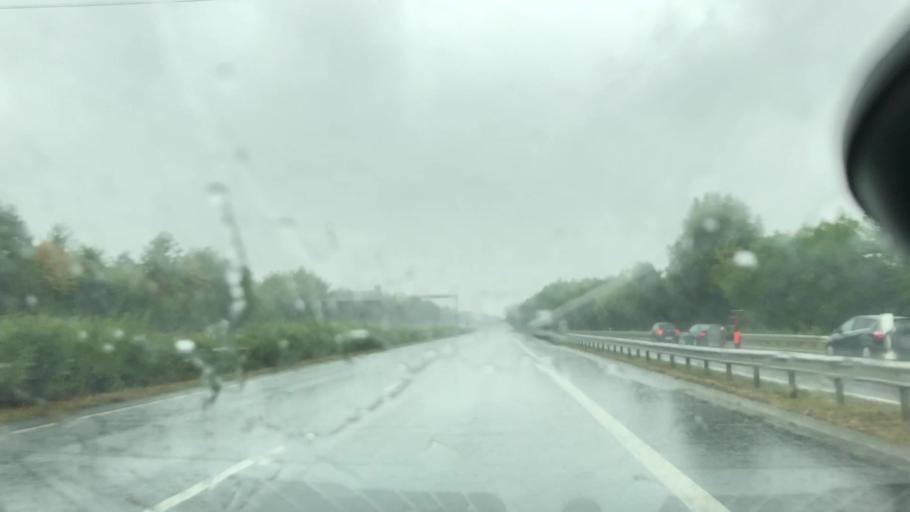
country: DE
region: North Rhine-Westphalia
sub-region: Regierungsbezirk Detmold
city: Minden
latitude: 52.2681
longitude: 8.9112
